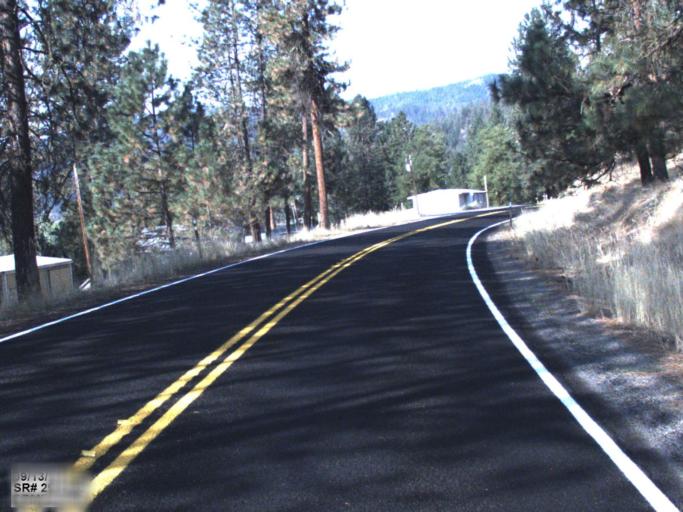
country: US
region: Washington
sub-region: Spokane County
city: Deer Park
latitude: 47.8912
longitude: -117.6732
